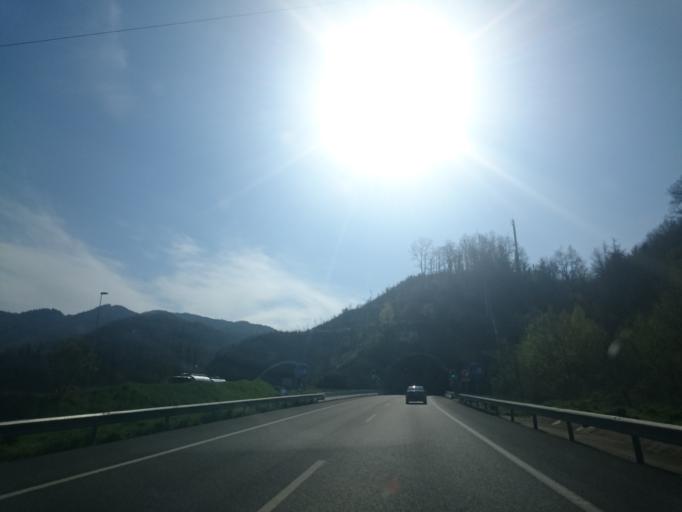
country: ES
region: Catalonia
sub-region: Provincia de Girona
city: Viladrau
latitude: 41.8666
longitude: 2.4144
